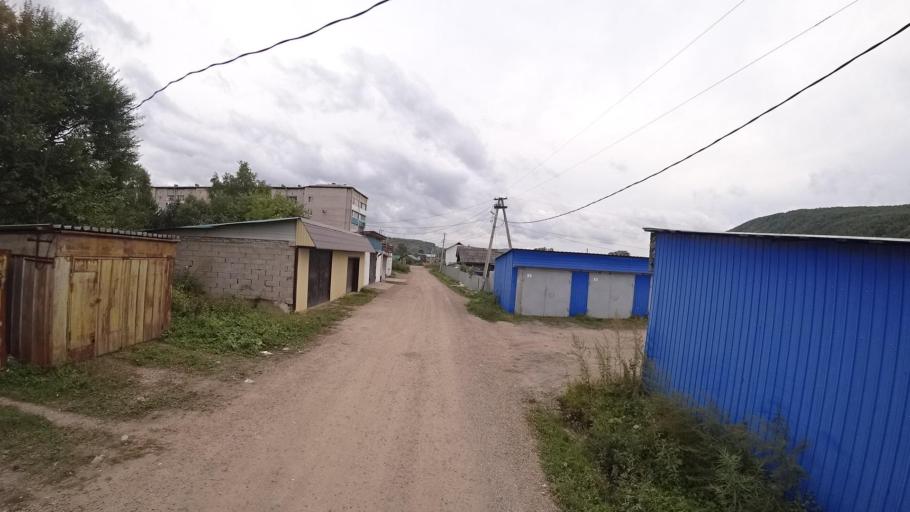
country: RU
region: Jewish Autonomous Oblast
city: Khingansk
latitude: 49.0095
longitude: 131.0502
